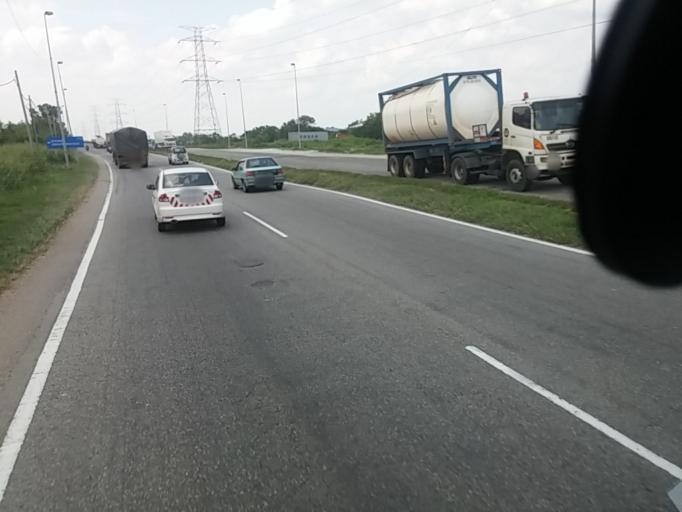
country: MY
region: Selangor
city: Klang
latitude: 2.9778
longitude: 101.3976
